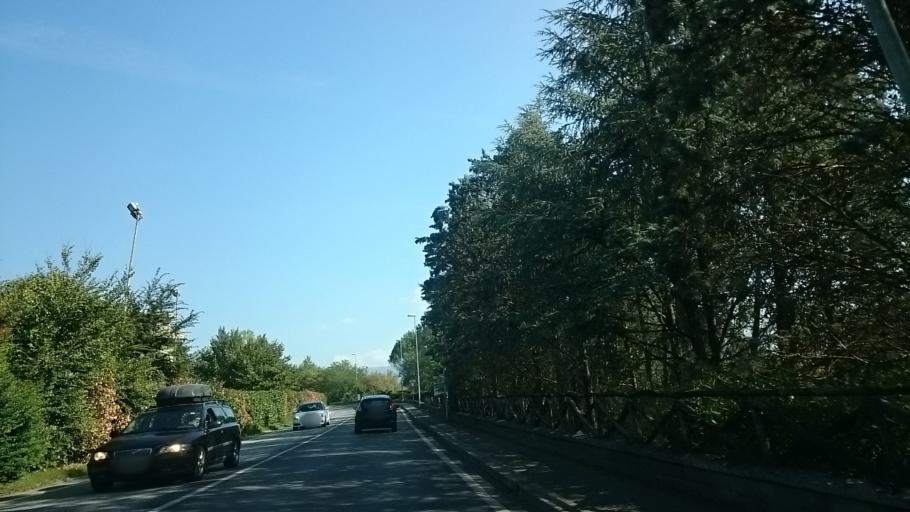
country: IT
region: Tuscany
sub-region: Province of Florence
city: Incisa in Val d'Arno
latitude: 43.6499
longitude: 11.4666
